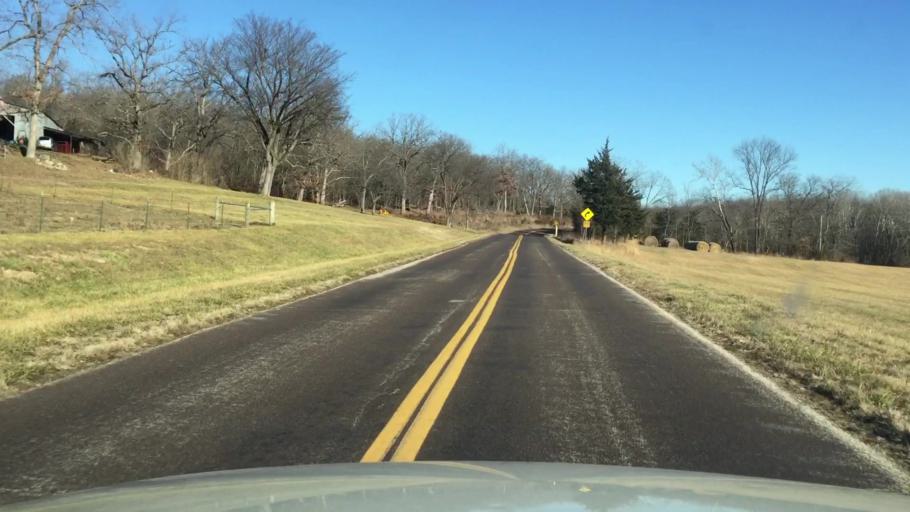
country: US
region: Missouri
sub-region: Miller County
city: Eldon
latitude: 38.3392
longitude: -92.7144
